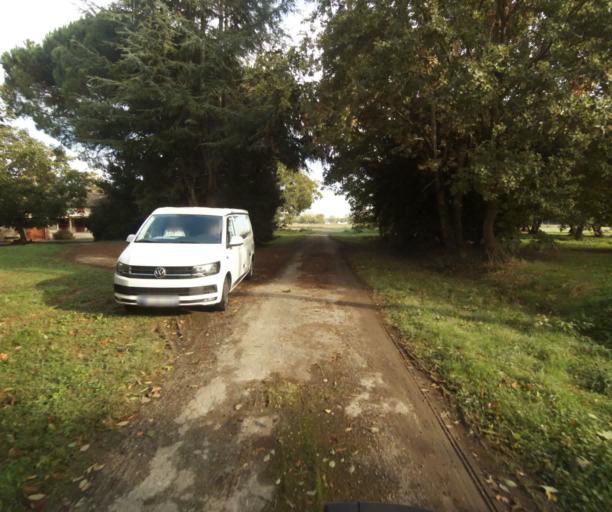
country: FR
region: Midi-Pyrenees
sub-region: Departement du Tarn-et-Garonne
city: Montech
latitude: 43.9704
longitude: 1.2280
